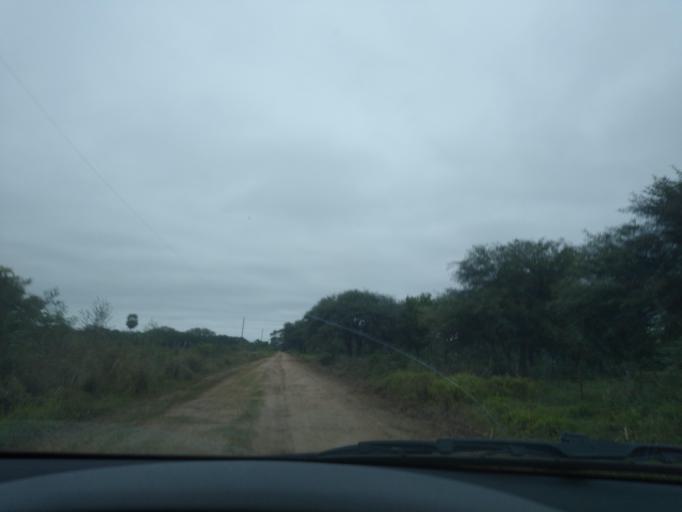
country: AR
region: Chaco
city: Colonia Benitez
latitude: -27.3753
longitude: -58.9429
